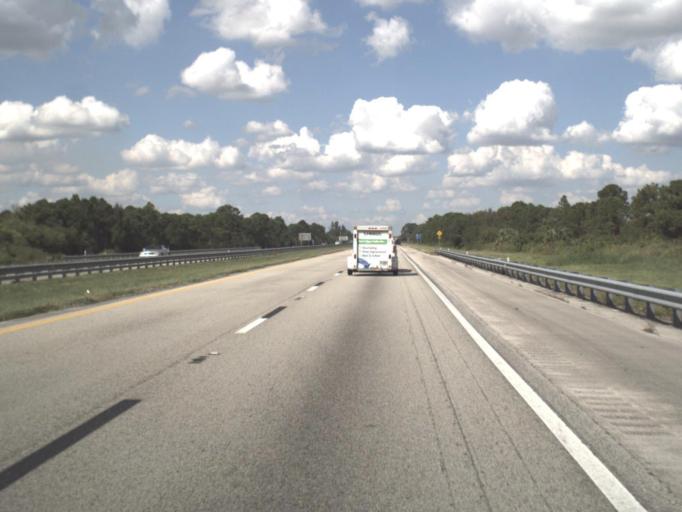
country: US
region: Florida
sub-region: Saint Lucie County
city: Fort Pierce South
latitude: 27.4249
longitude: -80.4115
